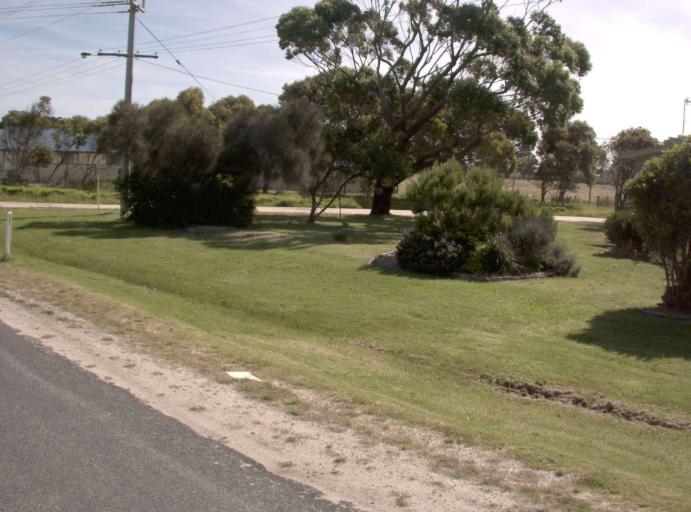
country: AU
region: Victoria
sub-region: Wellington
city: Sale
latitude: -38.3731
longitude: 147.1881
